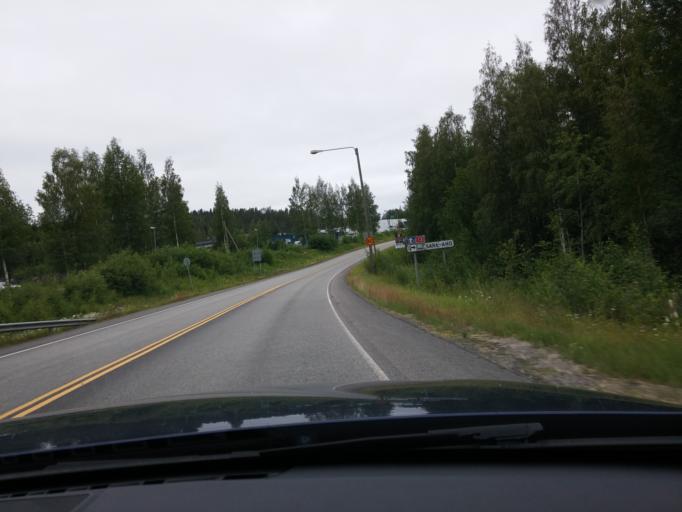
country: FI
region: Central Finland
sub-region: Saarijaervi-Viitasaari
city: Saarijaervi
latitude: 62.6874
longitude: 25.3129
